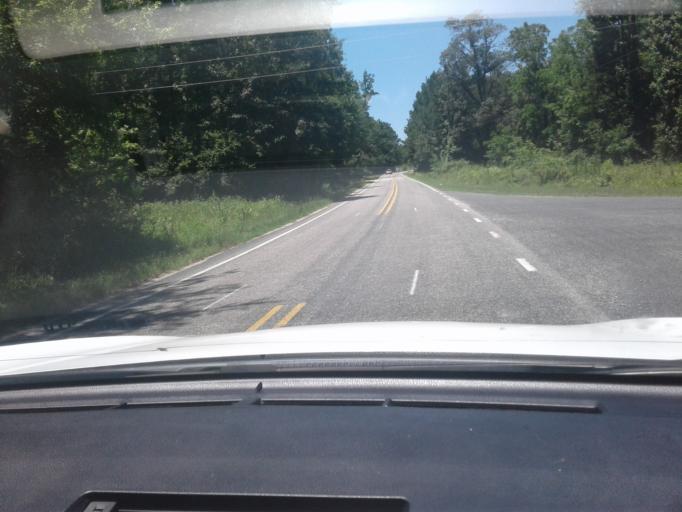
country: US
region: North Carolina
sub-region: Harnett County
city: Lillington
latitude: 35.3472
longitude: -78.9078
